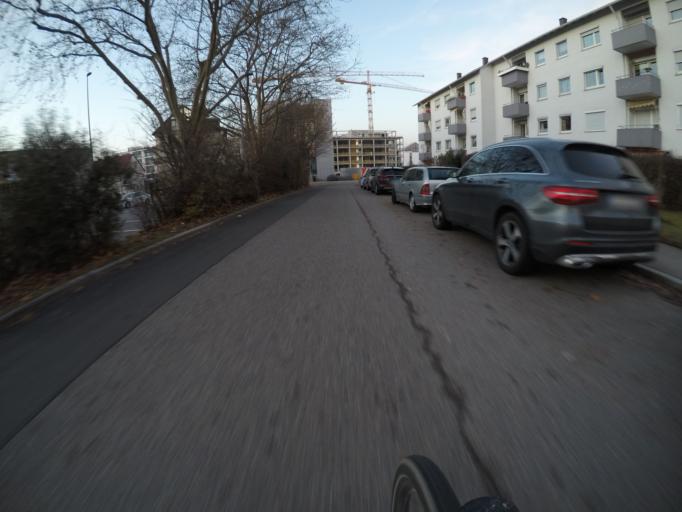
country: DE
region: Baden-Wuerttemberg
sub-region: Regierungsbezirk Stuttgart
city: Leinfelden-Echterdingen
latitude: 48.7054
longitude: 9.1450
